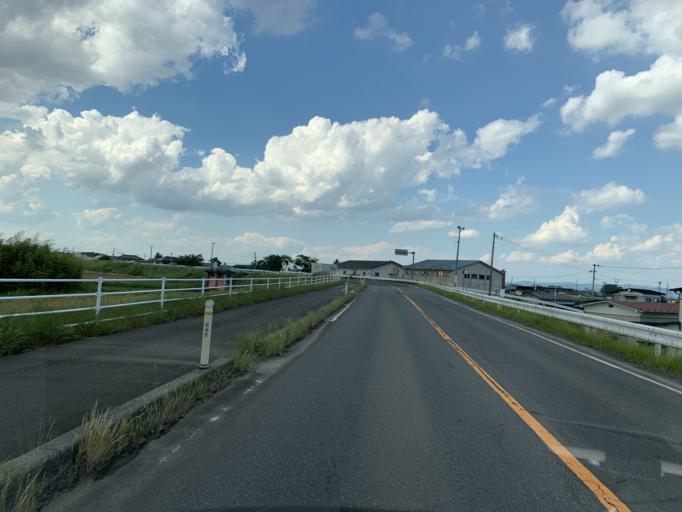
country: JP
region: Miyagi
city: Wakuya
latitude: 38.6495
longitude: 141.2174
